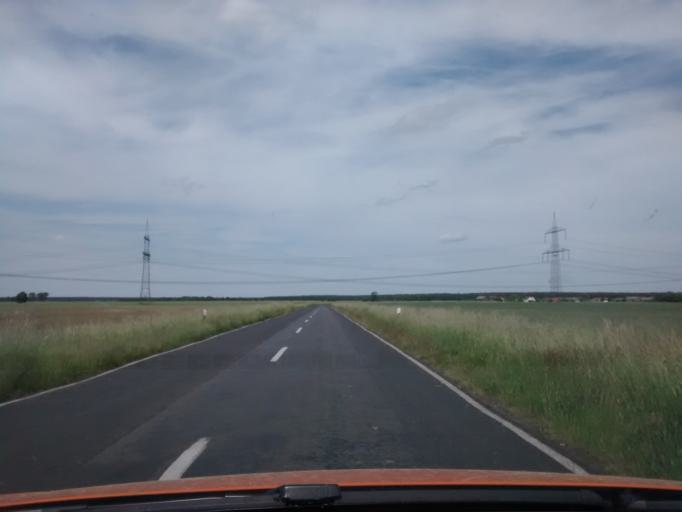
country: DE
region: Brandenburg
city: Ihlow
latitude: 51.8315
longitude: 13.2394
